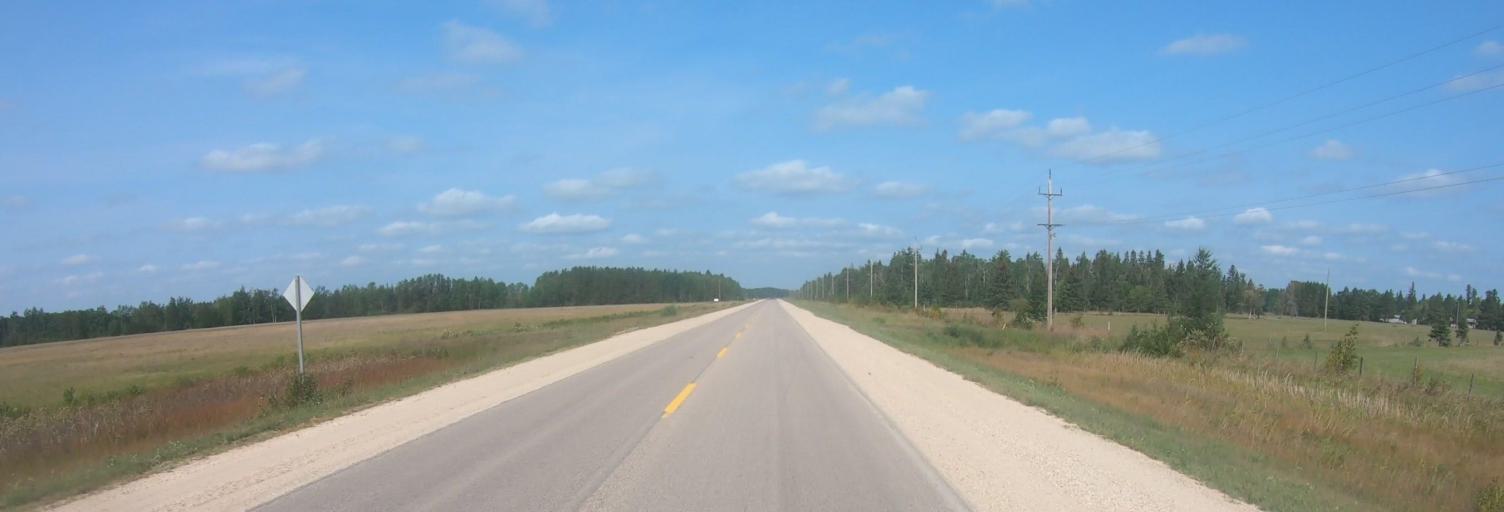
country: CA
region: Manitoba
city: La Broquerie
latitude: 49.1800
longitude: -96.2341
